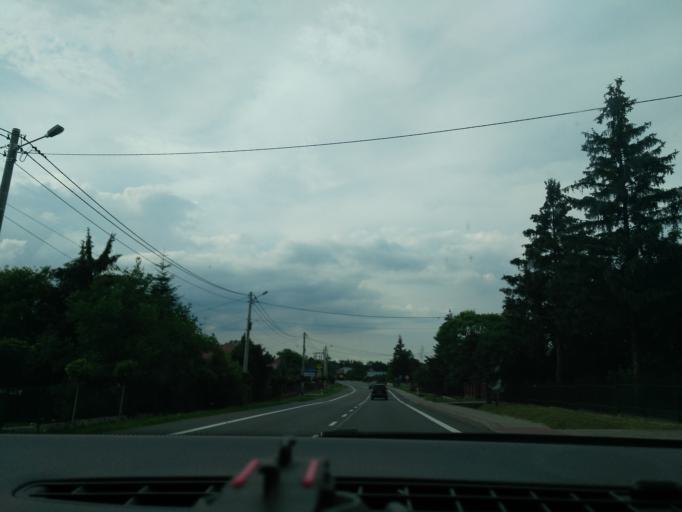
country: PL
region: Subcarpathian Voivodeship
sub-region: Powiat rzeszowski
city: Kamien
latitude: 50.3383
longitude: 22.1360
